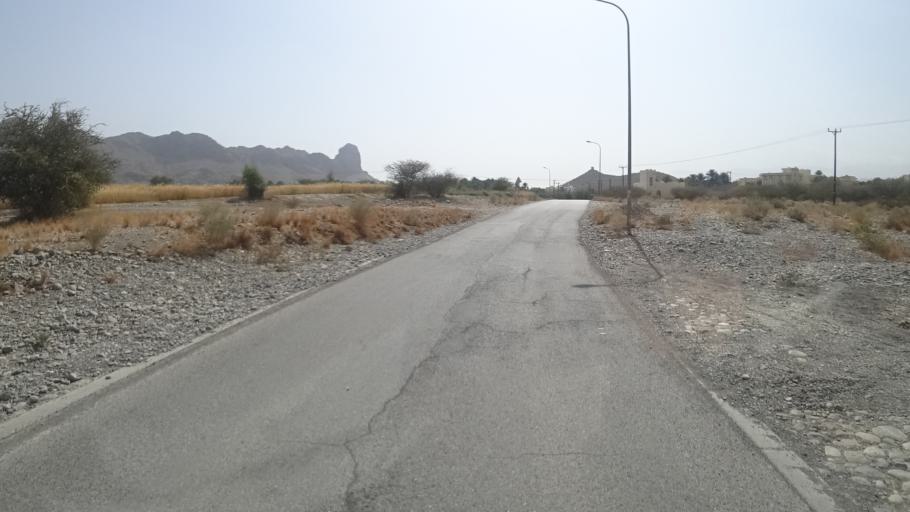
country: OM
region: Muhafazat ad Dakhiliyah
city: Bahla'
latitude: 23.1004
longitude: 57.3034
